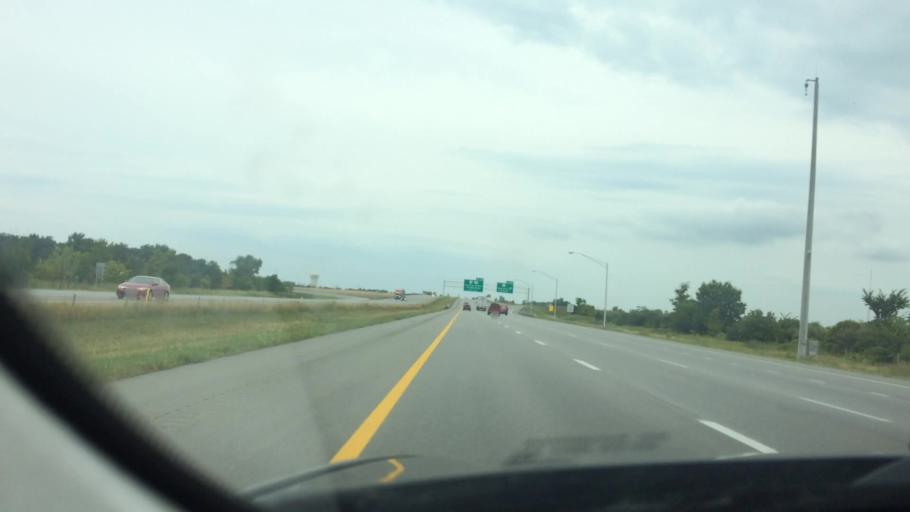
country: US
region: Ohio
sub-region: Wood County
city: Bowling Green
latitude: 41.3451
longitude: -83.6260
